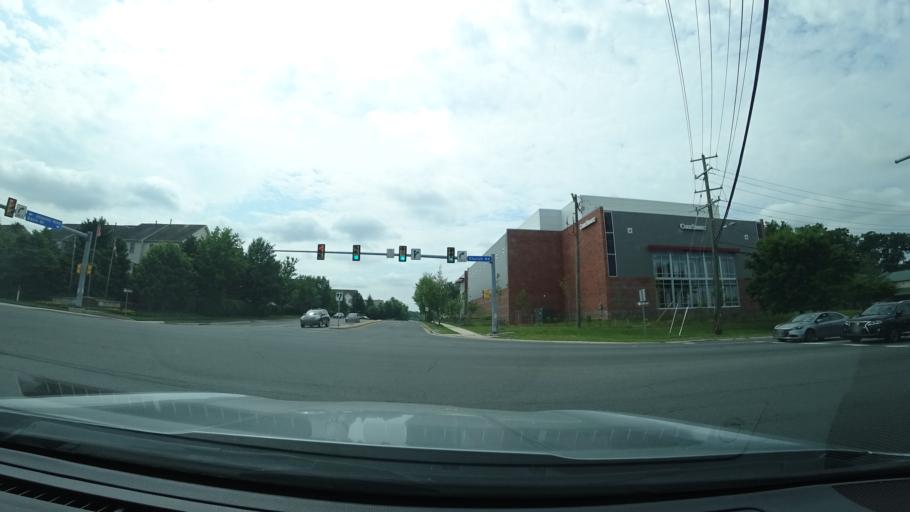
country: US
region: Virginia
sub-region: Loudoun County
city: Sterling
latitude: 39.0051
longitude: -77.4293
